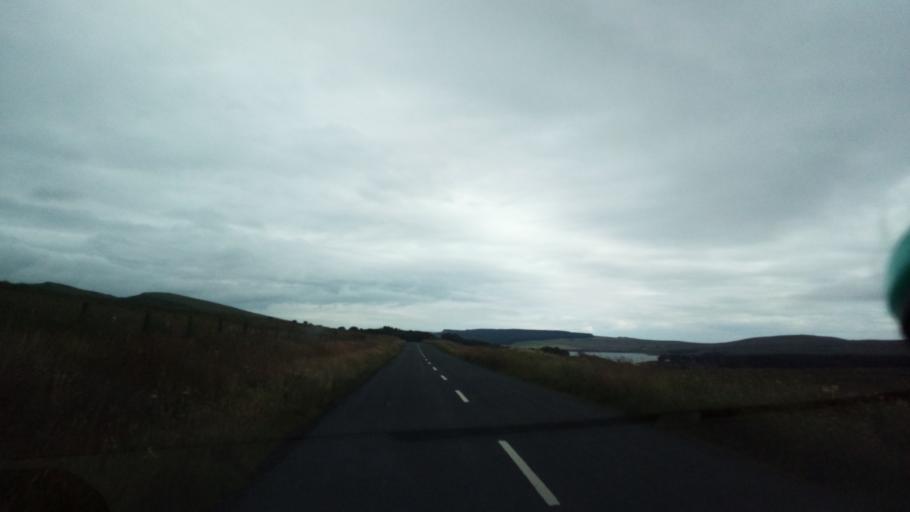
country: GB
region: England
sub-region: County Durham
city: Holwick
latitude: 54.5915
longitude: -2.1745
